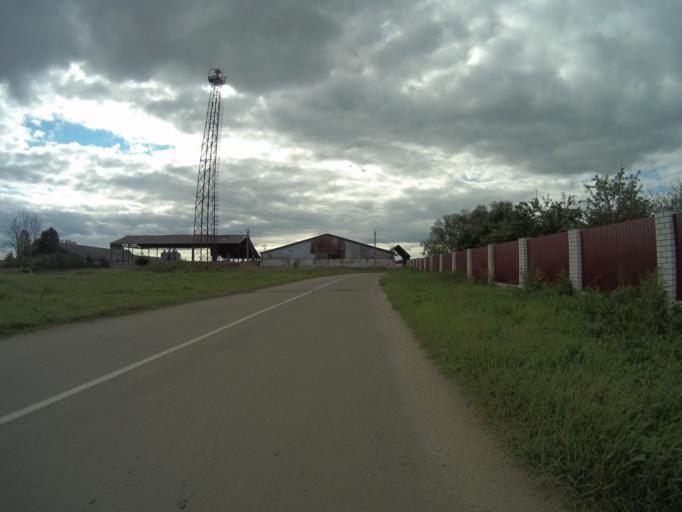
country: RU
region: Vladimir
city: Orgtrud
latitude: 56.3091
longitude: 40.6065
